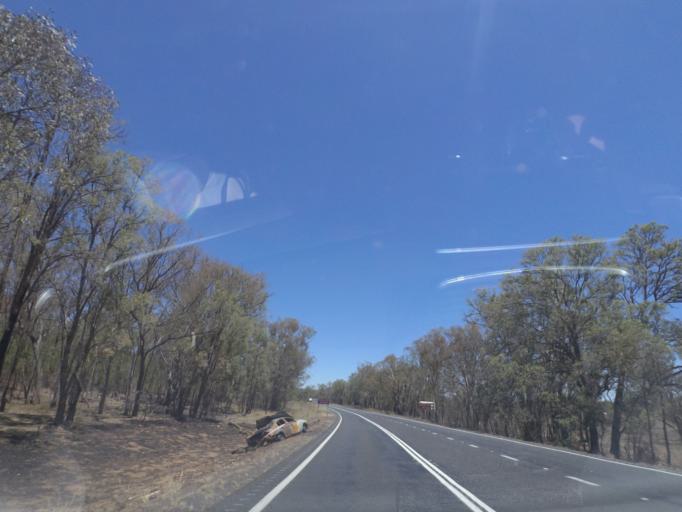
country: AU
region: New South Wales
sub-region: Warrumbungle Shire
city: Coonabarabran
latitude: -31.2398
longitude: 149.3140
